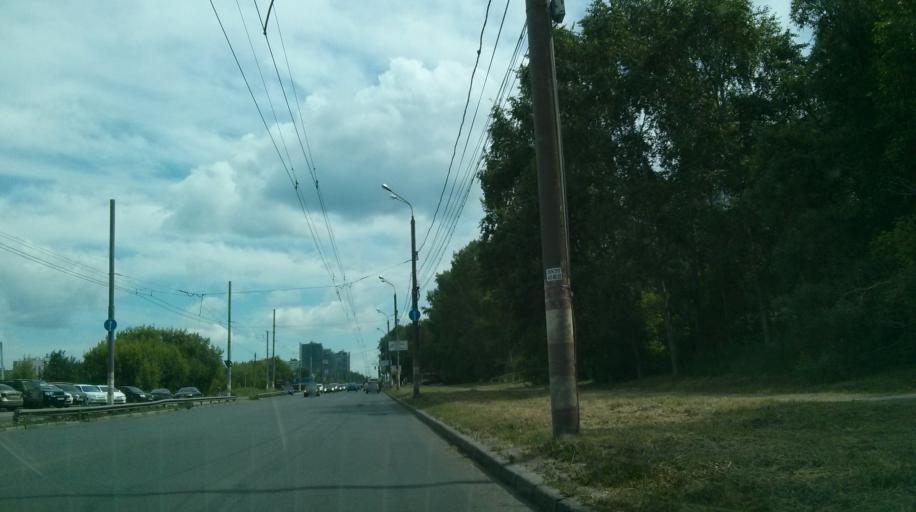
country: RU
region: Nizjnij Novgorod
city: Afonino
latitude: 56.2998
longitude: 44.0644
